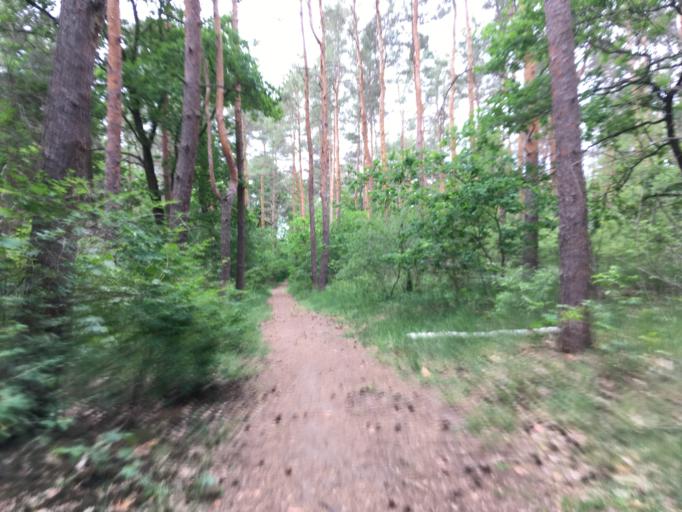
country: DE
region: Berlin
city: Karlshorst
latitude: 52.4778
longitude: 13.5546
